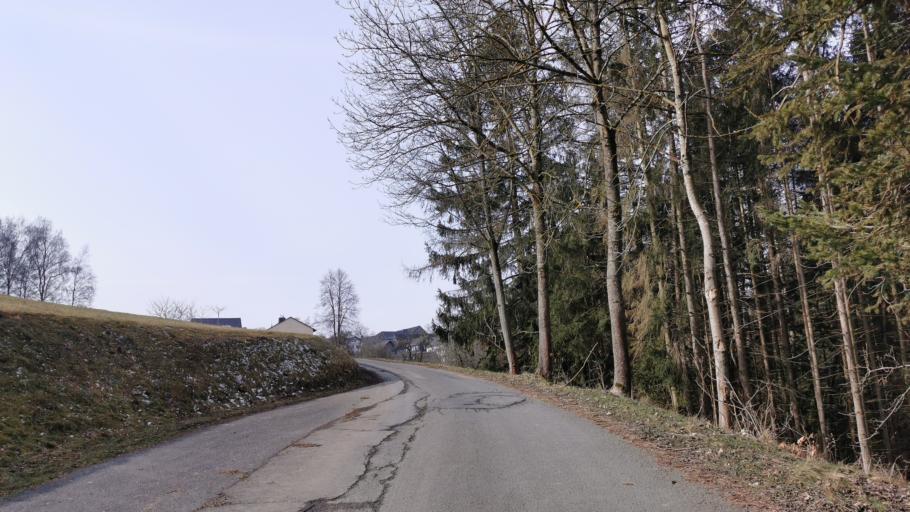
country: DE
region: Bavaria
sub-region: Upper Franconia
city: Ludwigsstadt
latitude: 50.5100
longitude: 11.4237
